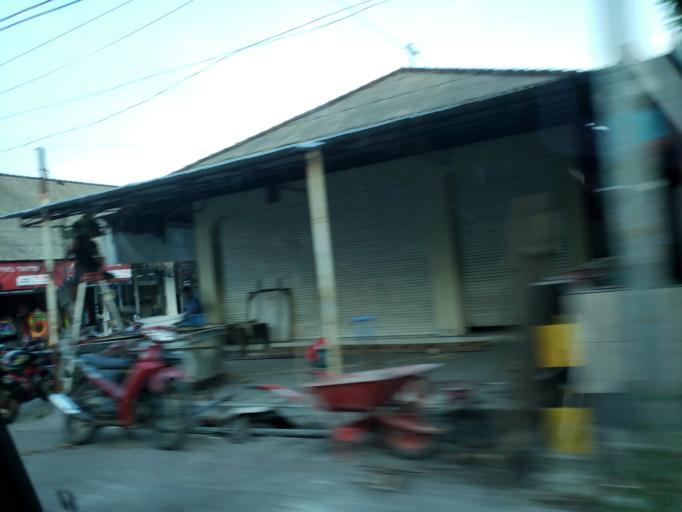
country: ID
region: Bali
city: Jimbaran
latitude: -8.8033
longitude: 115.1598
